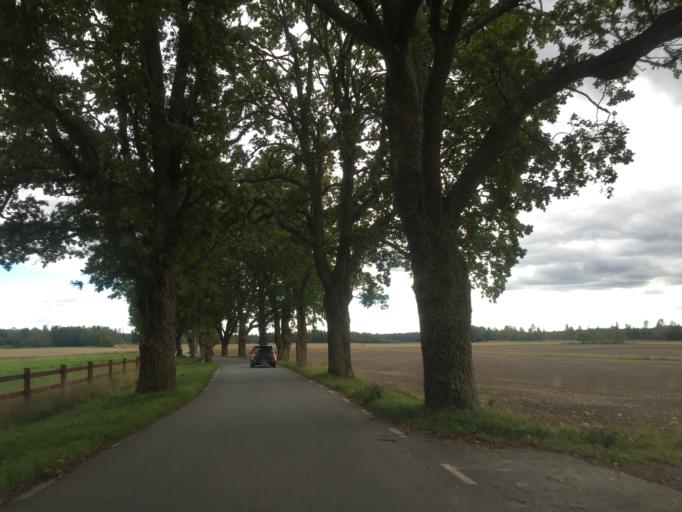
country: SE
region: OErebro
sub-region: Orebro Kommun
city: Hovsta
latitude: 59.3462
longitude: 15.1689
